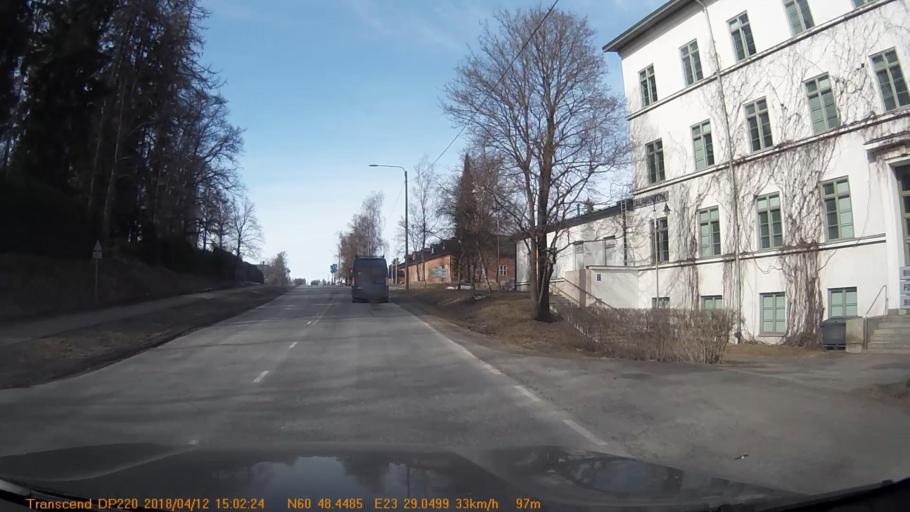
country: FI
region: Haeme
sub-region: Forssa
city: Jokioinen
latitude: 60.8076
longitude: 23.4841
